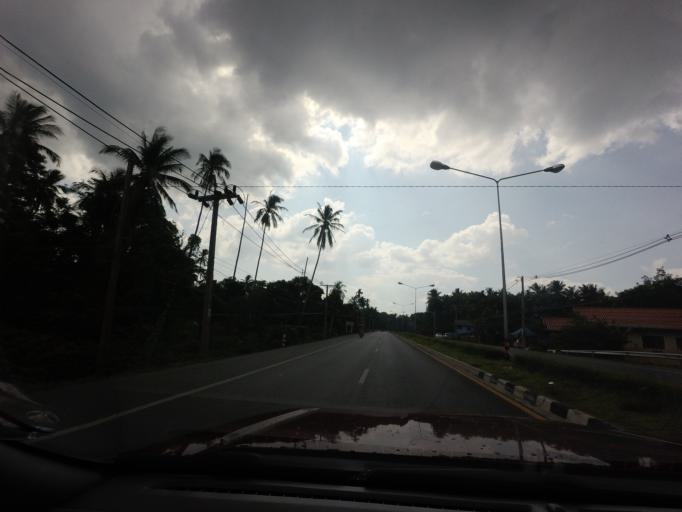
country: TH
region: Yala
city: Krong Pi Nang
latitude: 6.4694
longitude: 101.2689
